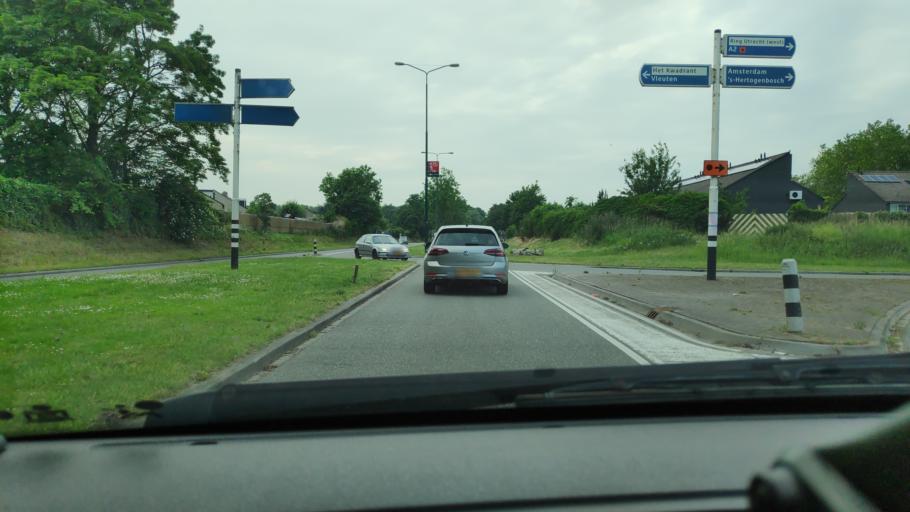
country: NL
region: Utrecht
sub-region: Stichtse Vecht
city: Maarssen
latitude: 52.1238
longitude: 5.0321
